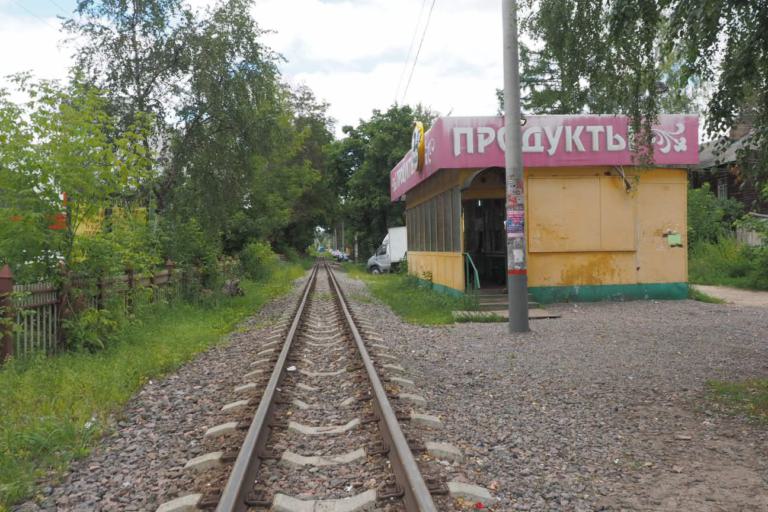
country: RU
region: Moskovskaya
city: Zhukovskiy
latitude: 55.5876
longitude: 38.1421
